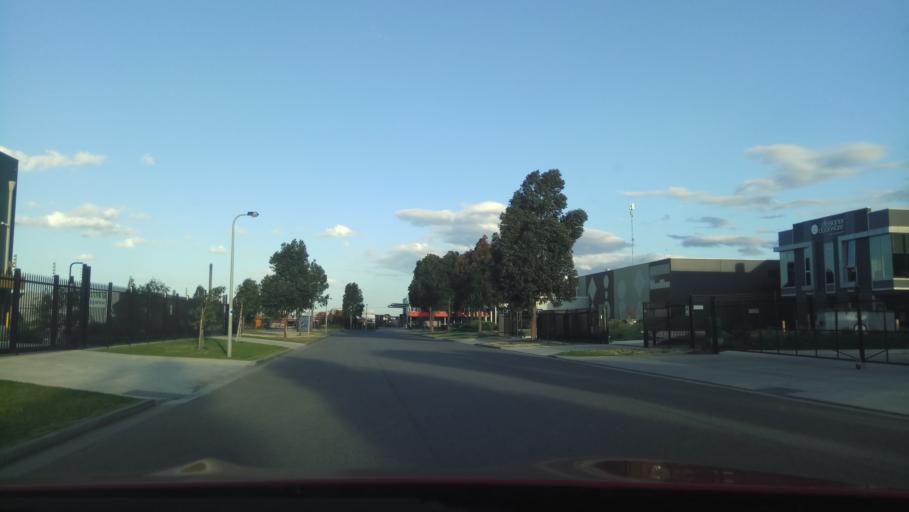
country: AU
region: Victoria
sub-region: Hobsons Bay
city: Seaholme
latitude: -37.8510
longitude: 144.8320
